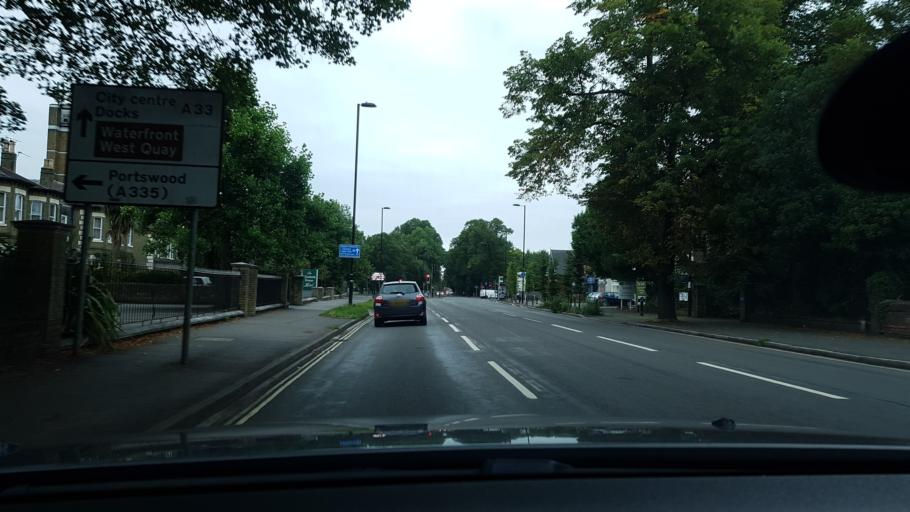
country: GB
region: England
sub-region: Southampton
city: Southampton
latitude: 50.9199
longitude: -1.4043
